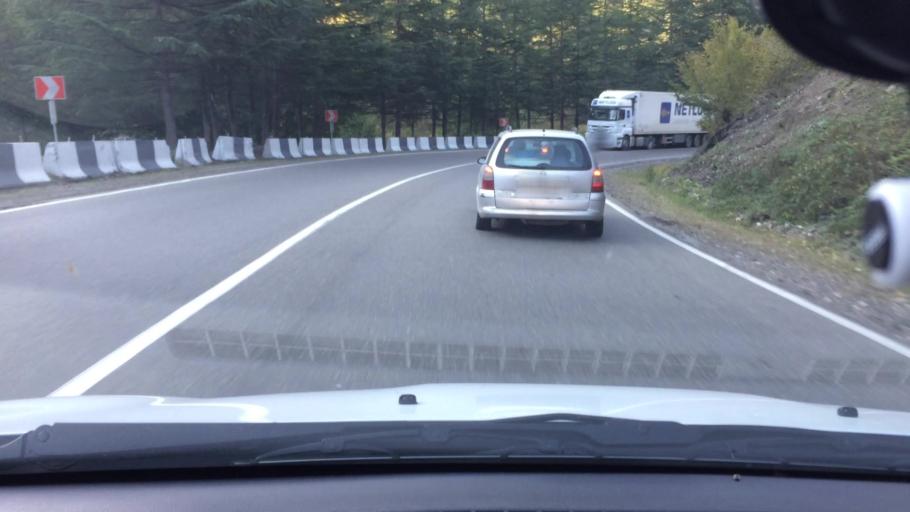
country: GE
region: Imereti
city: Kharagauli
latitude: 42.0910
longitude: 43.1680
